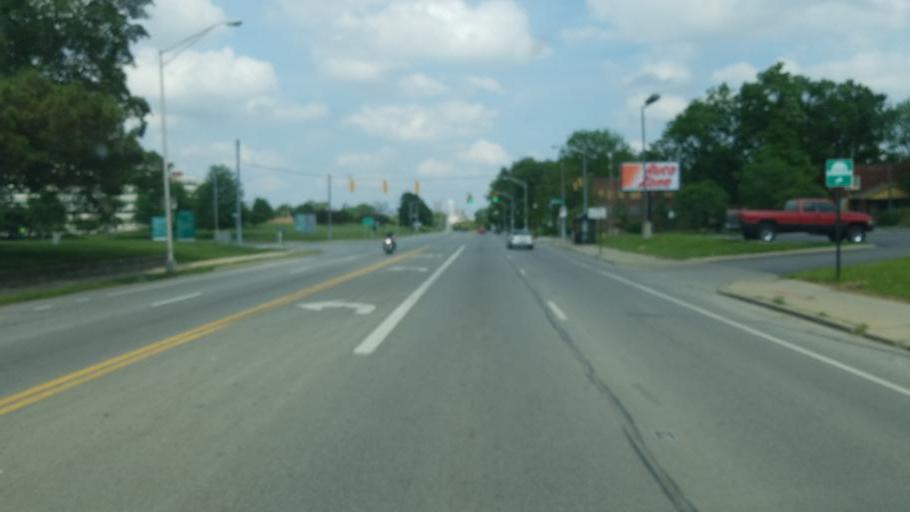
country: US
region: Ohio
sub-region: Franklin County
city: Grandview Heights
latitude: 39.9557
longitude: -83.0577
